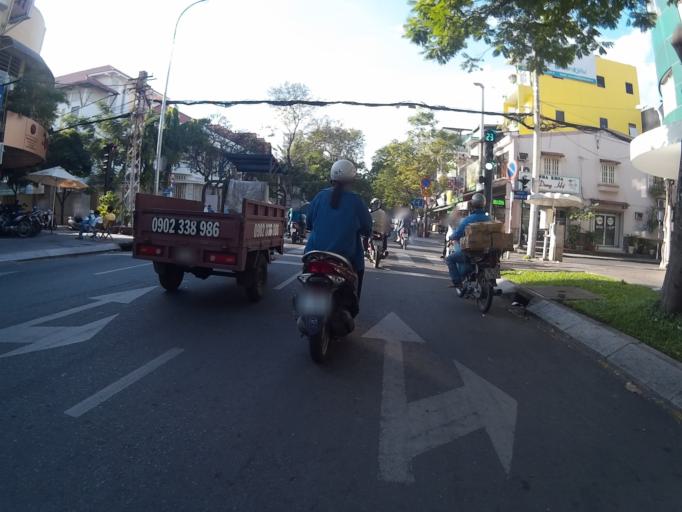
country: VN
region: Ho Chi Minh City
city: Quan Mot
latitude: 10.7893
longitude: 106.6987
